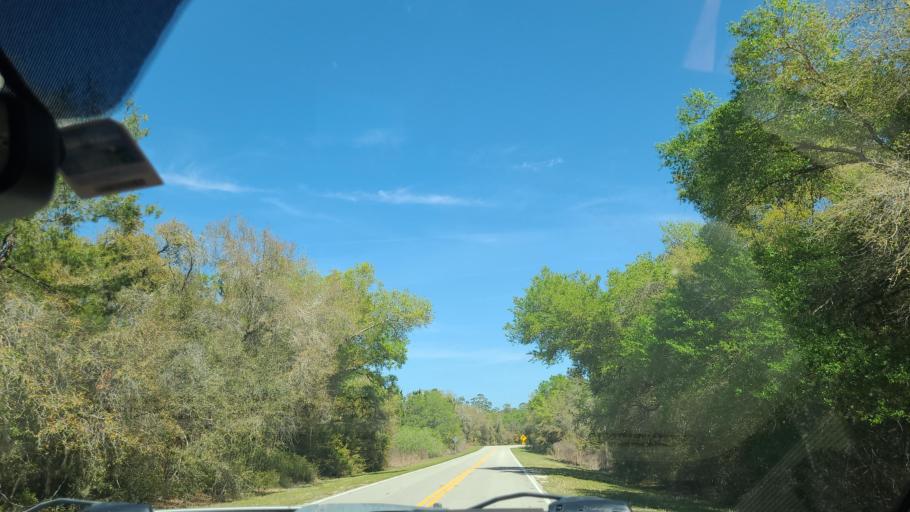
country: US
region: Florida
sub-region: Putnam County
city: Crescent City
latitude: 29.3787
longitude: -81.7723
